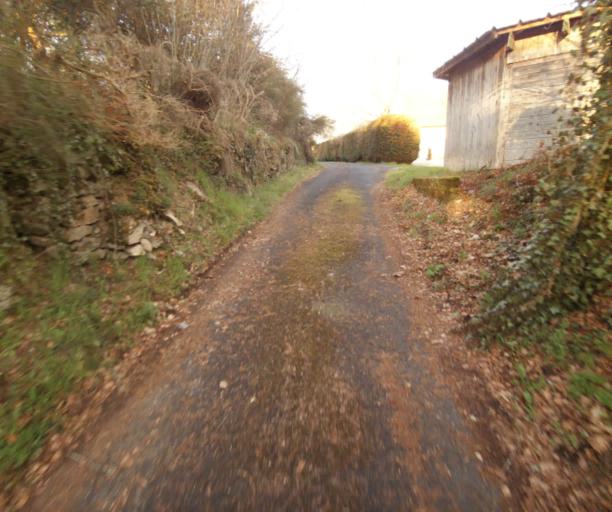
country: FR
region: Limousin
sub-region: Departement de la Correze
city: Argentat
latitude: 45.2455
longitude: 1.9808
